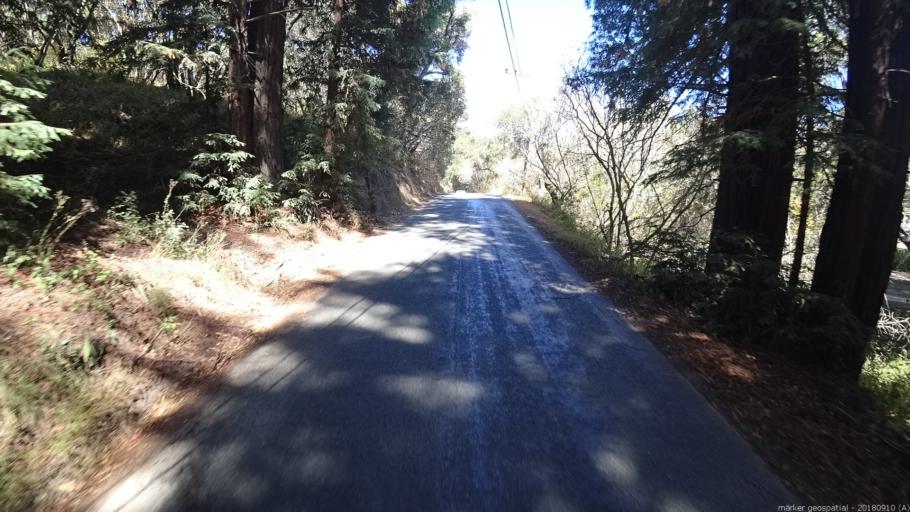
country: US
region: California
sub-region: Monterey County
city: Carmel Valley Village
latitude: 36.5152
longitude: -121.8129
